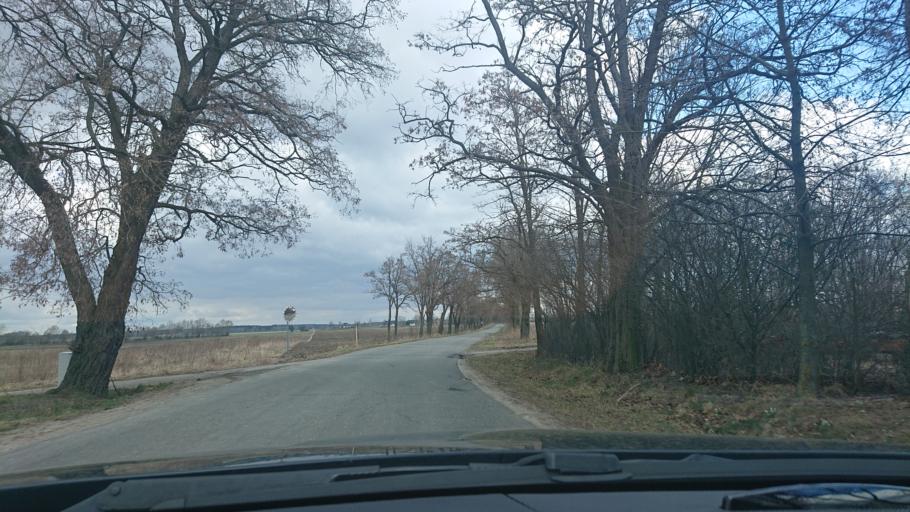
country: PL
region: Greater Poland Voivodeship
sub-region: Powiat gnieznienski
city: Niechanowo
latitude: 52.5744
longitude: 17.7057
